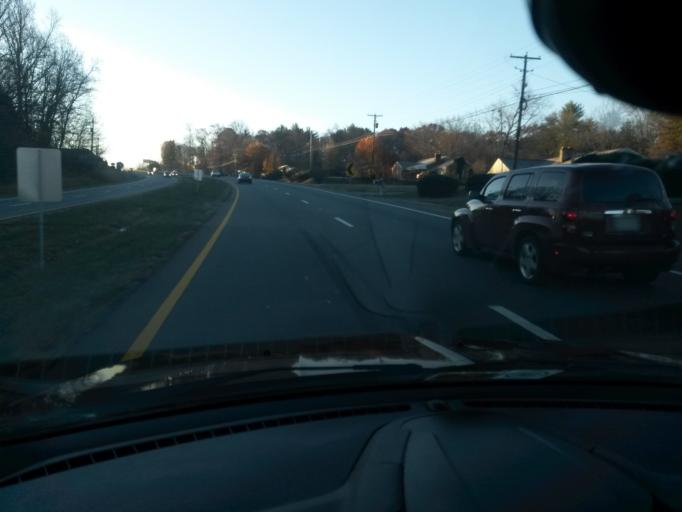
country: US
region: Virginia
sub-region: Franklin County
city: Rocky Mount
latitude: 37.0503
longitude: -79.8817
